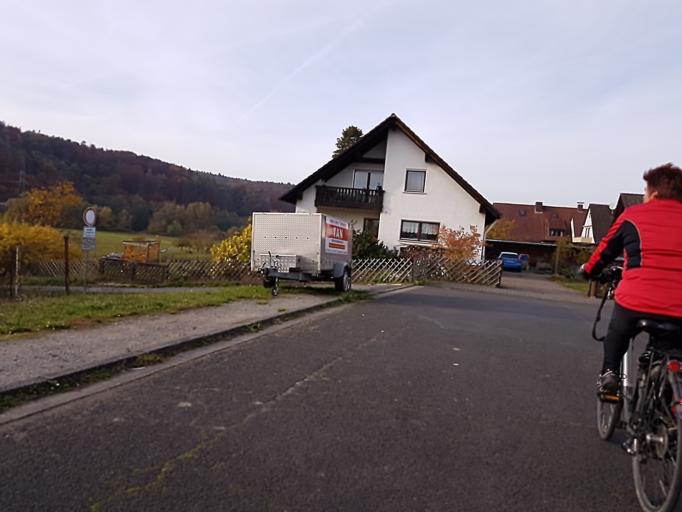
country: DE
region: Bavaria
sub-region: Regierungsbezirk Unterfranken
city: Worth am Main
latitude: 49.8079
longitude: 9.1412
